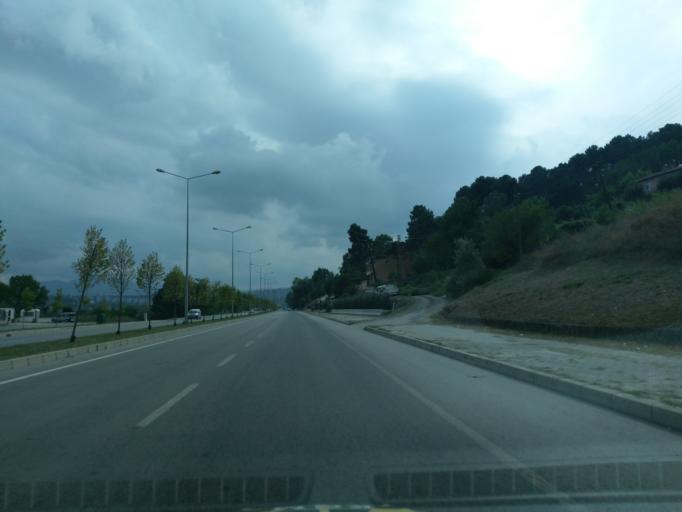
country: TR
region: Samsun
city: Samsun
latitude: 41.3075
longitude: 36.2987
